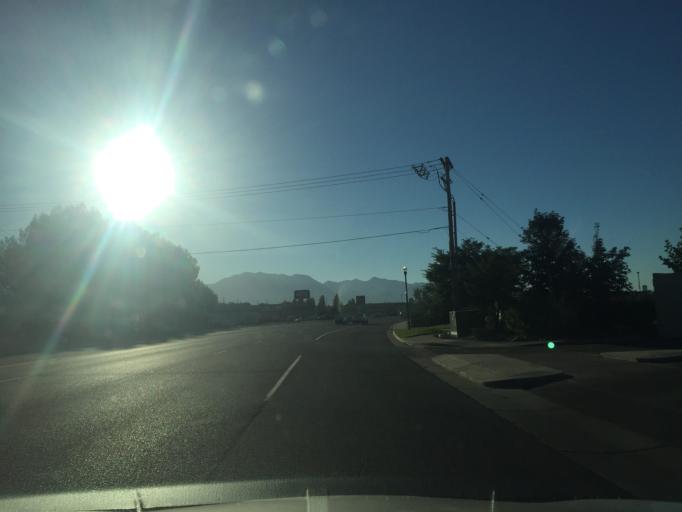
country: US
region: Utah
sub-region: Utah County
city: American Fork
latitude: 40.3848
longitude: -111.8172
